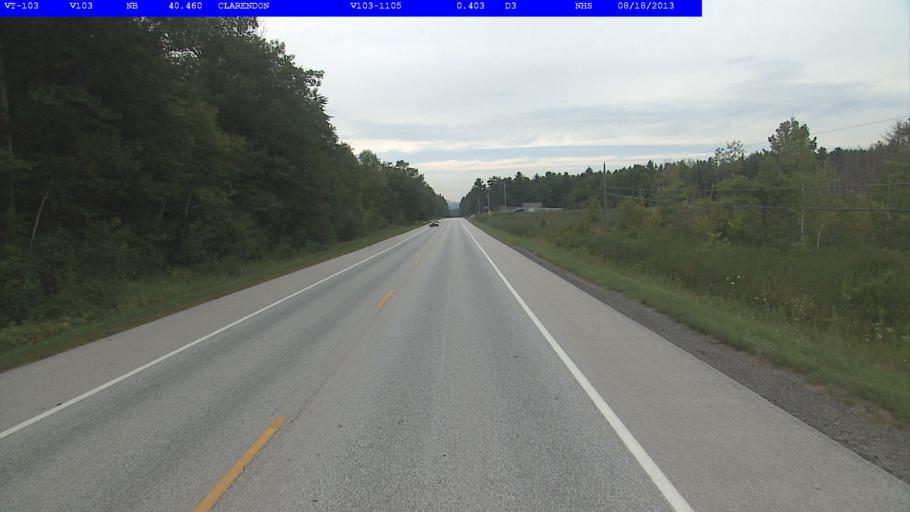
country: US
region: Vermont
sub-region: Rutland County
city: Rutland
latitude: 43.5286
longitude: -72.9353
